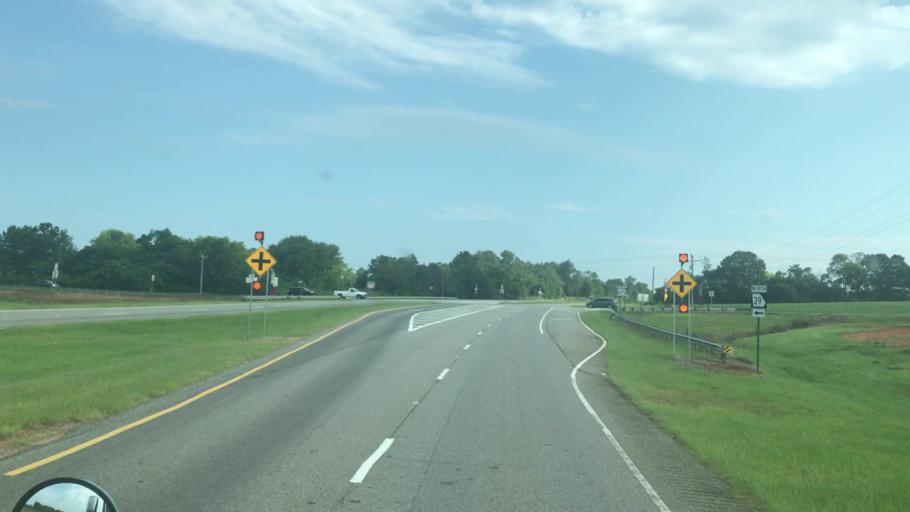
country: US
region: Georgia
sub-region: Early County
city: Blakely
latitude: 31.3903
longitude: -84.9241
